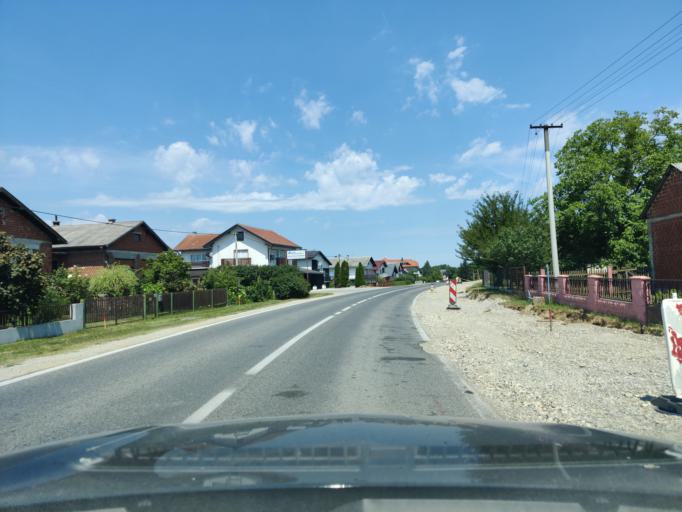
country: HR
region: Medimurska
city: Mackovec
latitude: 46.4409
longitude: 16.4307
